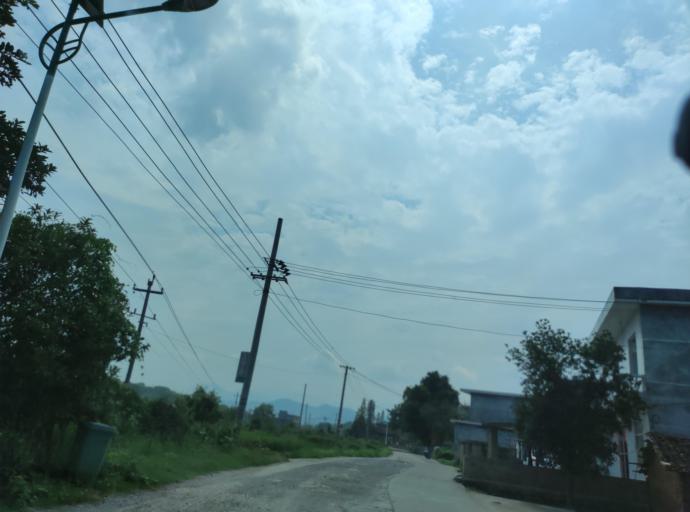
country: CN
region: Jiangxi Sheng
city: Yuannan
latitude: 27.6695
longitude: 114.0400
